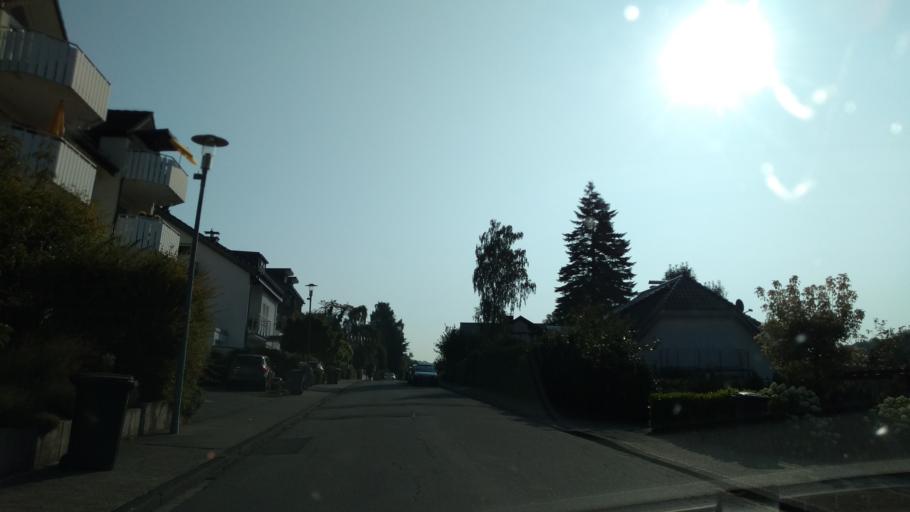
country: DE
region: North Rhine-Westphalia
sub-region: Regierungsbezirk Arnsberg
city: Luedenscheid
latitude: 51.2132
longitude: 7.6044
